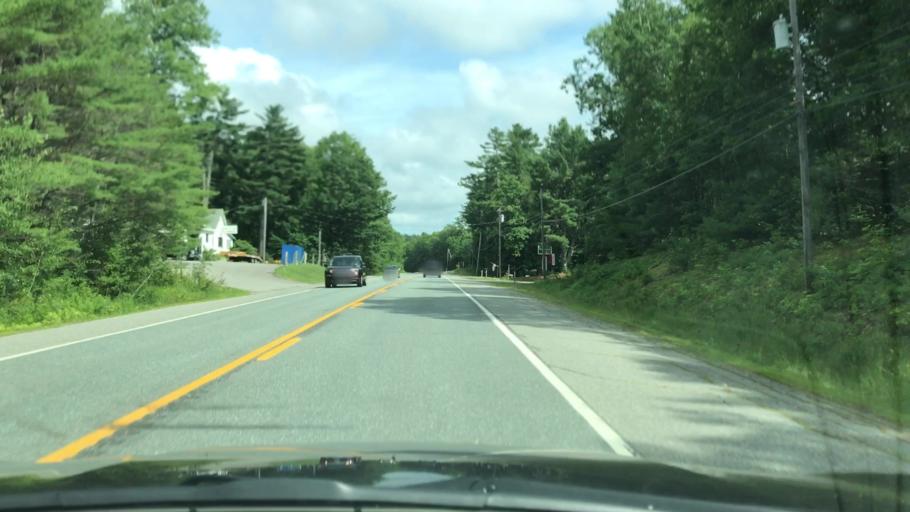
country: US
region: Maine
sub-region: Hancock County
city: Orland
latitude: 44.5658
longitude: -68.6697
